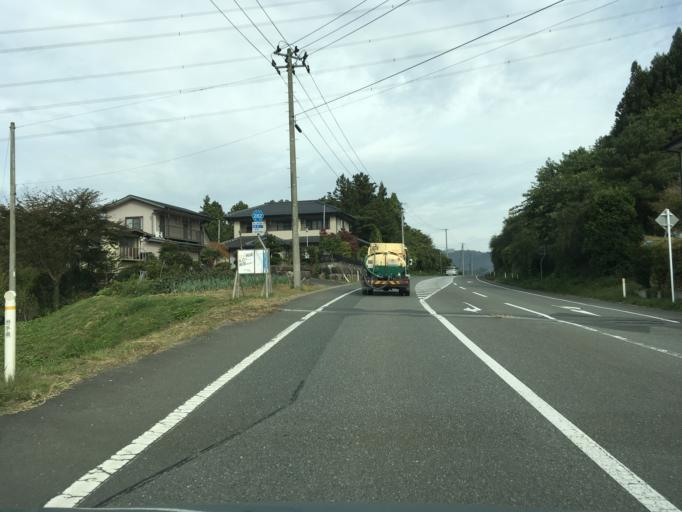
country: JP
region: Iwate
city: Ichinoseki
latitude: 38.9349
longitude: 141.2496
